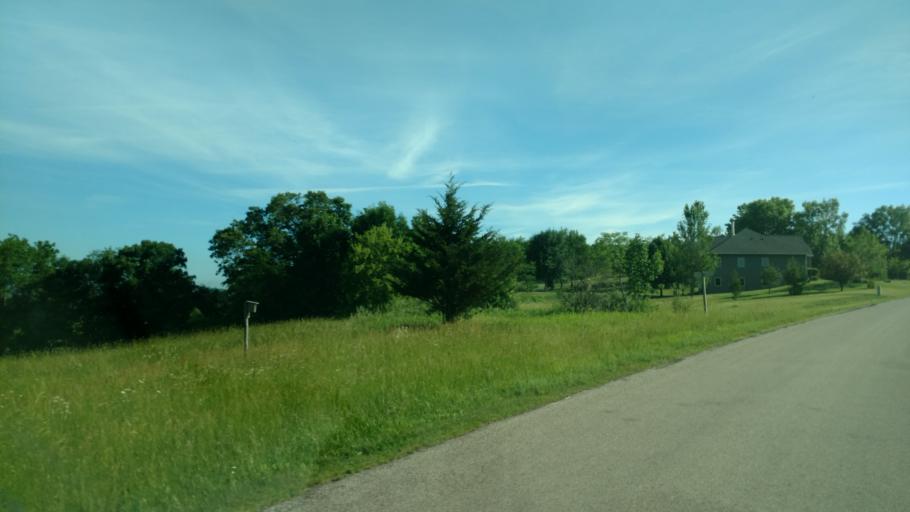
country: US
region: Wisconsin
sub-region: Vernon County
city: Hillsboro
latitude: 43.5867
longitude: -90.1826
